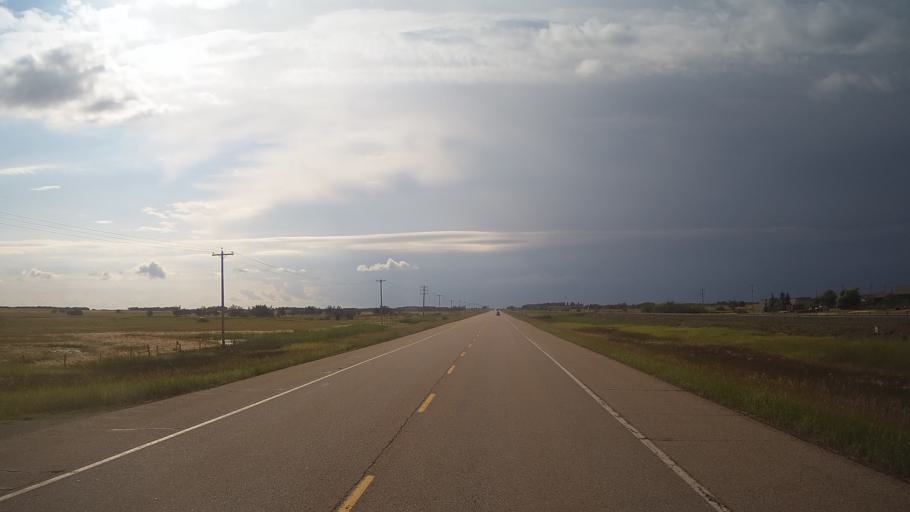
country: CA
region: Alberta
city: Viking
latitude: 53.1519
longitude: -111.9750
